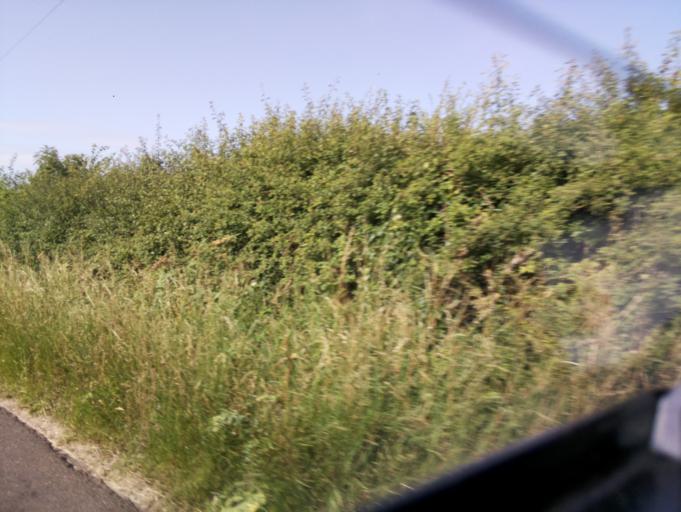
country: GB
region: England
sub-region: Oxfordshire
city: Ducklington
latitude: 51.7453
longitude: -1.4978
